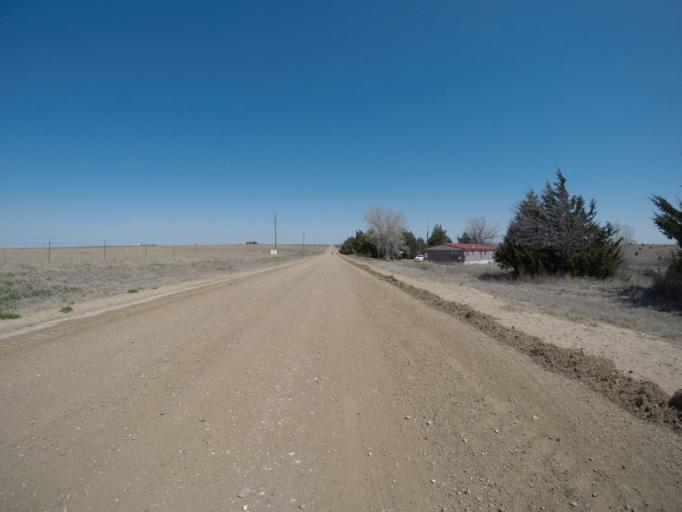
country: US
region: Kansas
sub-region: Pratt County
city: Pratt
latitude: 37.4205
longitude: -98.8388
